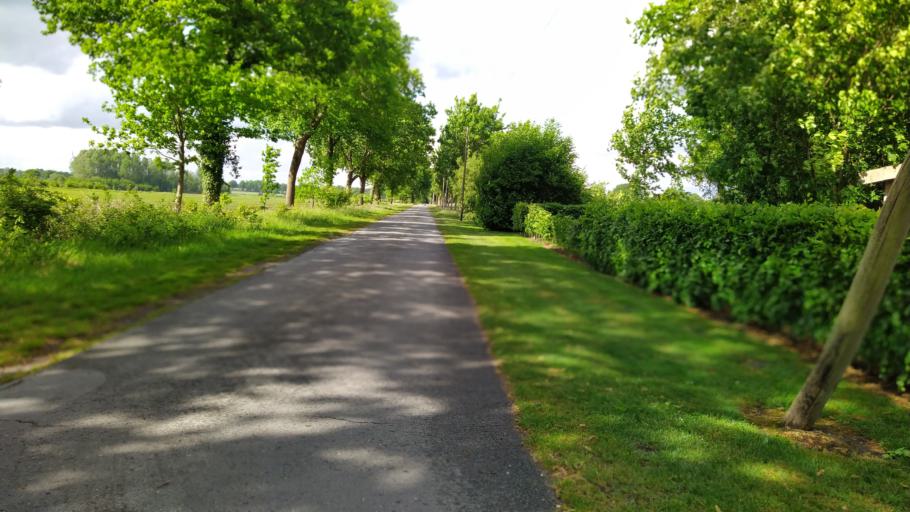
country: DE
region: Lower Saxony
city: Brest
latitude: 53.4524
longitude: 9.3912
